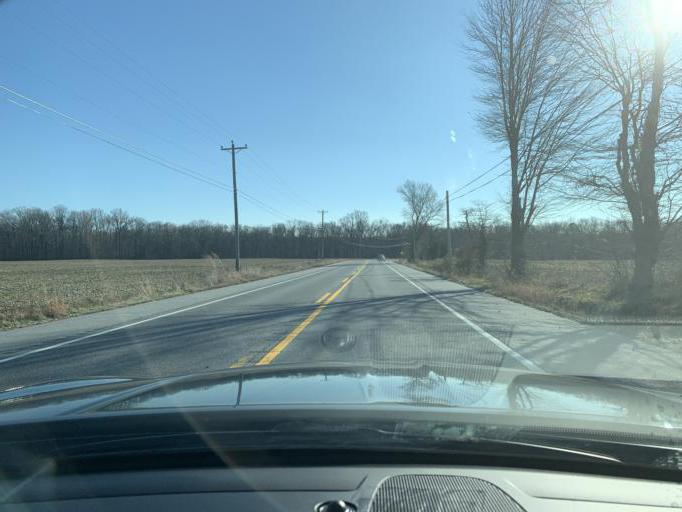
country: US
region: Maryland
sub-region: Queen Anne's County
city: Centreville
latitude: 39.0822
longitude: -76.0331
